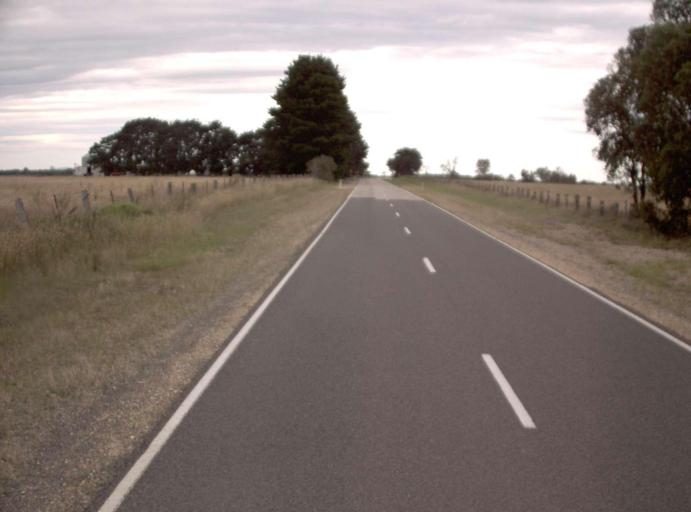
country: AU
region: Victoria
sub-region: East Gippsland
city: Bairnsdale
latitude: -37.9649
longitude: 147.4859
